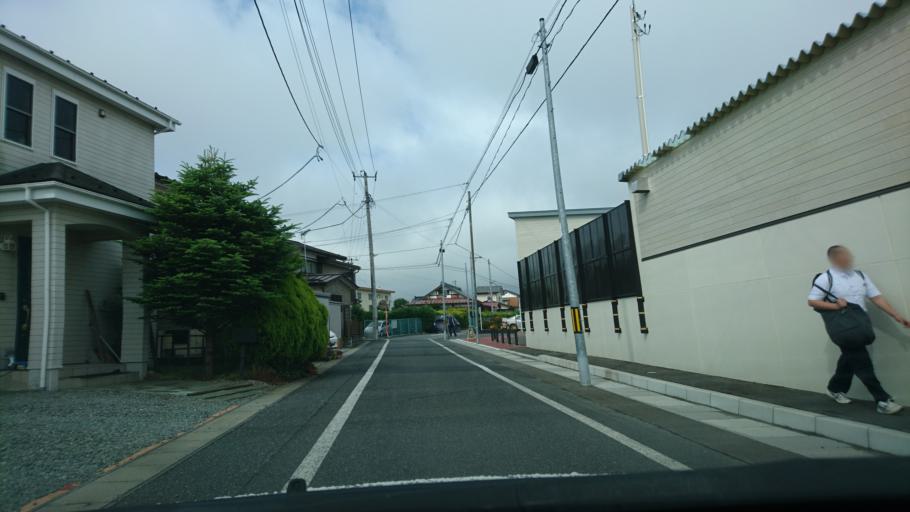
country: JP
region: Iwate
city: Ichinoseki
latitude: 38.9291
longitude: 141.1233
